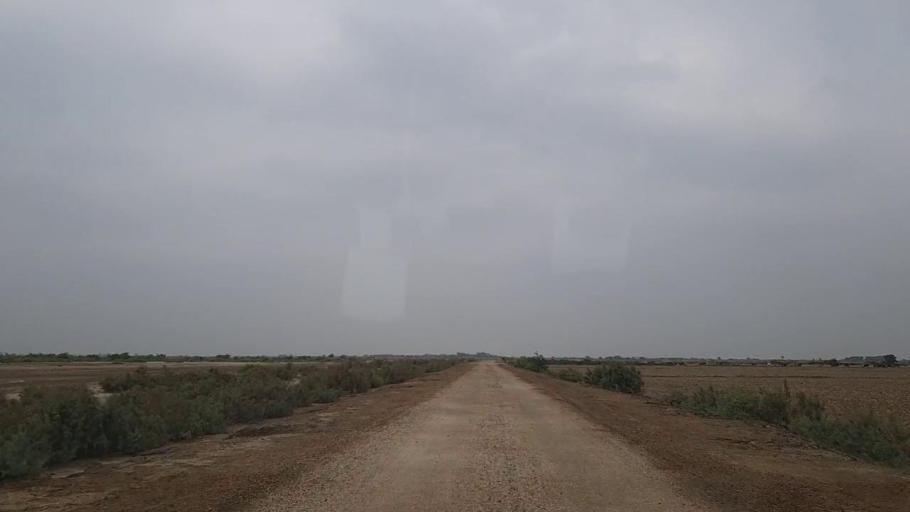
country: PK
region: Sindh
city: Mirpur Sakro
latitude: 24.6269
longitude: 67.7189
